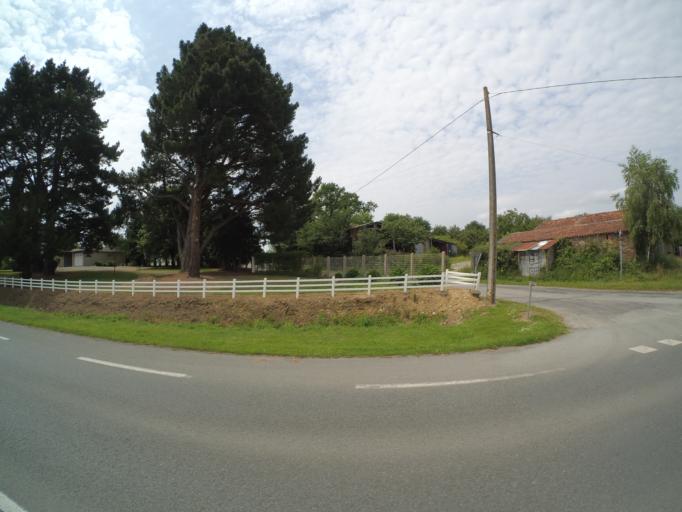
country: FR
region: Pays de la Loire
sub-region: Departement de la Vendee
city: Saint-Fulgent
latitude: 46.8665
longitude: -1.1929
